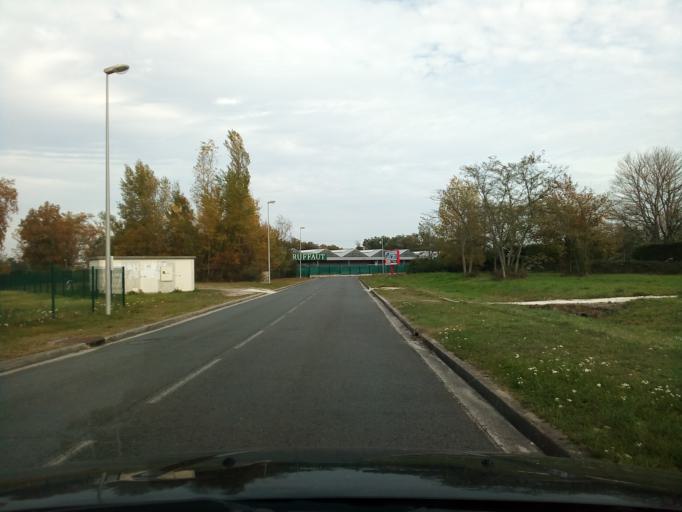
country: FR
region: Aquitaine
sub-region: Departement de la Gironde
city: Pessac
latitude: 44.8272
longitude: -0.6799
